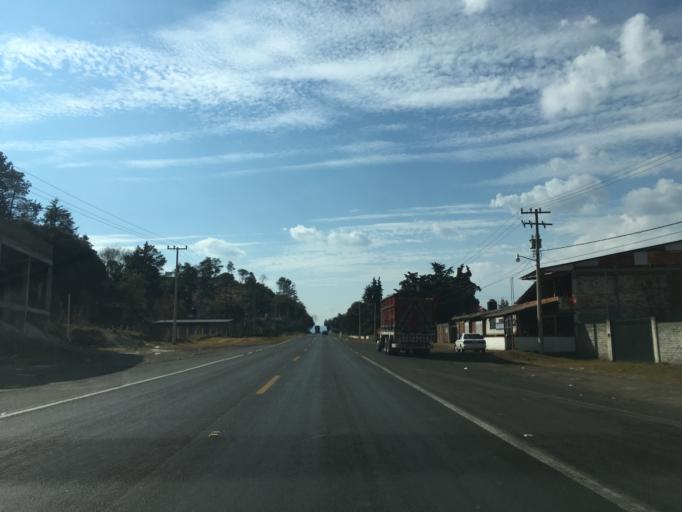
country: MX
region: Michoacan
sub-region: Patzcuaro
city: Santa Ana Chapitiro
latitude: 19.5327
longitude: -101.6292
